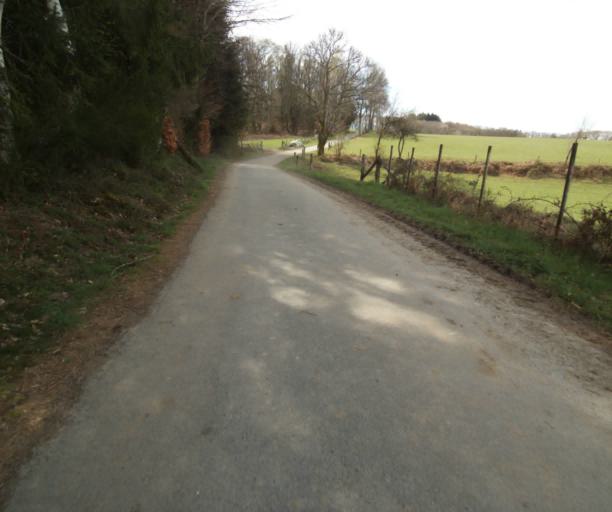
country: FR
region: Limousin
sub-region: Departement de la Correze
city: Correze
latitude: 45.3624
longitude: 1.9073
